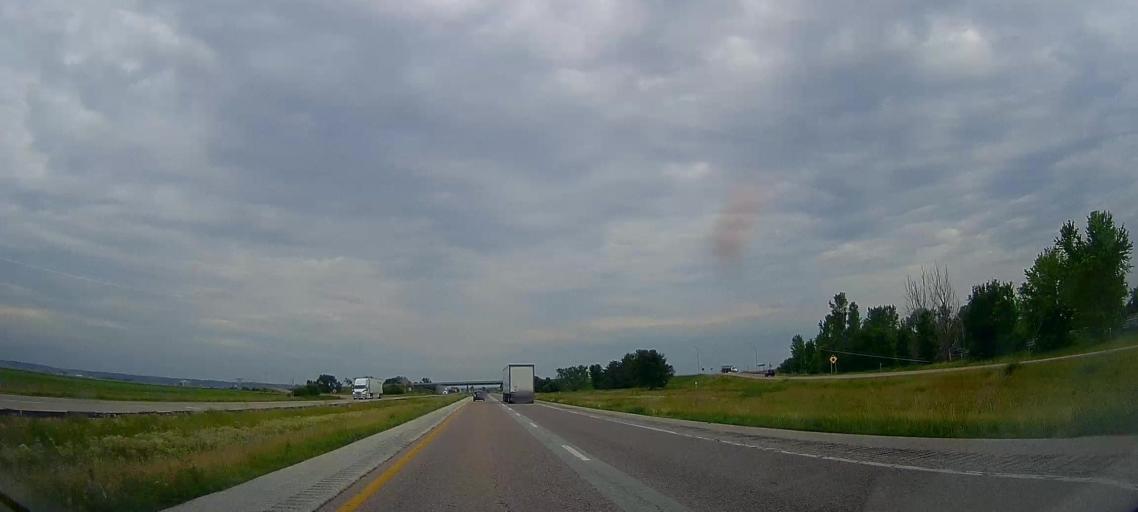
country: US
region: Iowa
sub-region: Harrison County
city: Missouri Valley
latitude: 41.6223
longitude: -95.9910
